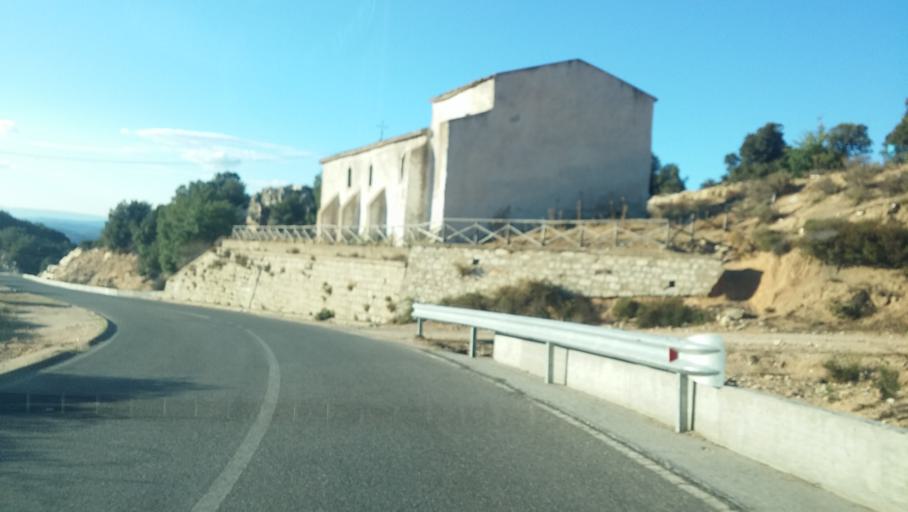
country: IT
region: Sardinia
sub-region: Provincia di Nuoro
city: Orgosolo
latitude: 40.1989
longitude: 9.3531
